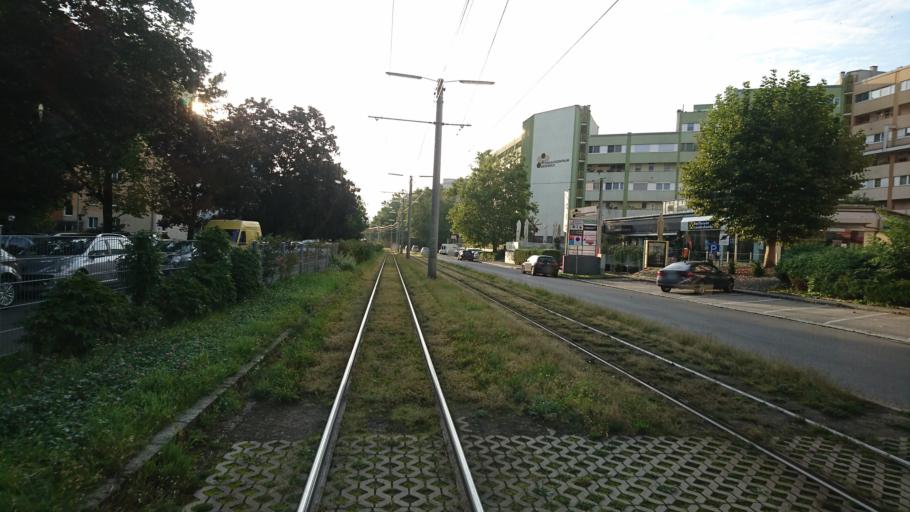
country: AT
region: Upper Austria
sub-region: Linz Stadt
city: Linz
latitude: 48.3325
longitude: 14.3096
